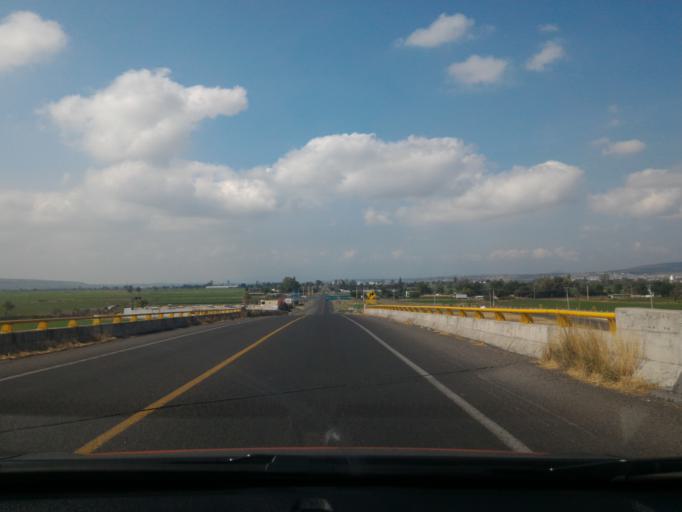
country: MX
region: Guanajuato
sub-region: Penjamo
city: Estacion la Piedad
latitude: 20.3950
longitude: -101.9998
